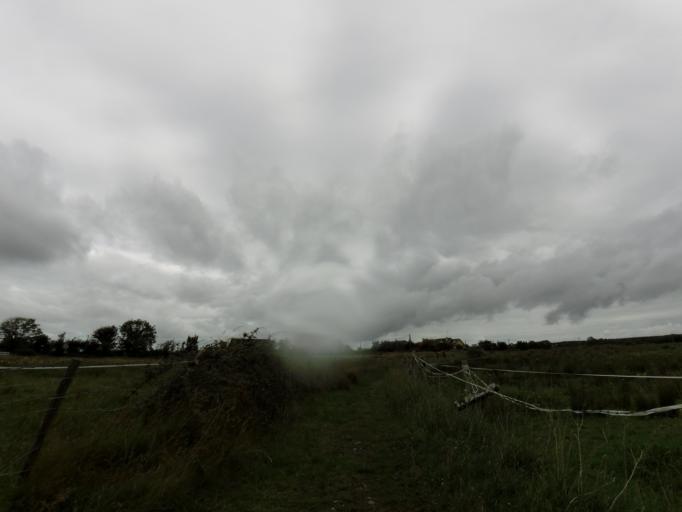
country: IE
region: Connaught
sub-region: County Galway
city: Athenry
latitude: 53.2865
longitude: -8.7123
